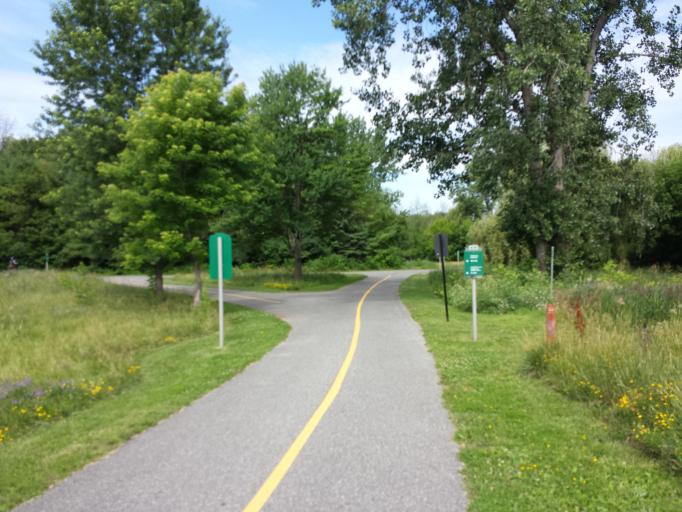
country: CA
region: Ontario
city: Bells Corners
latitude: 45.3716
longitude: -75.7858
